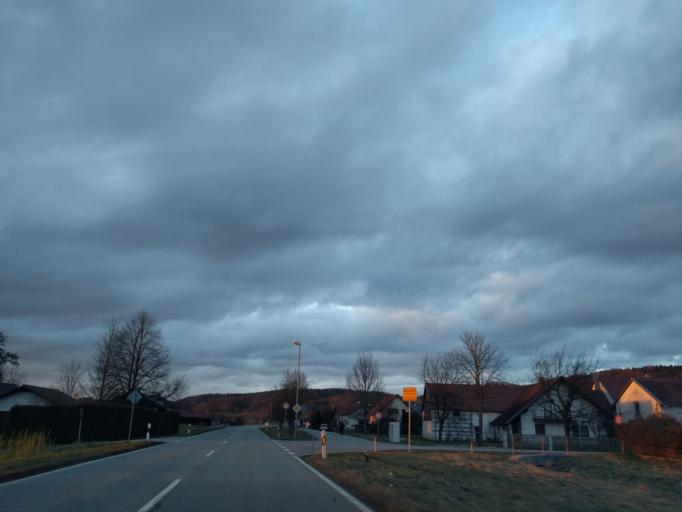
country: DE
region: Bavaria
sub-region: Lower Bavaria
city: Hofkirchen
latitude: 48.7053
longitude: 13.1089
